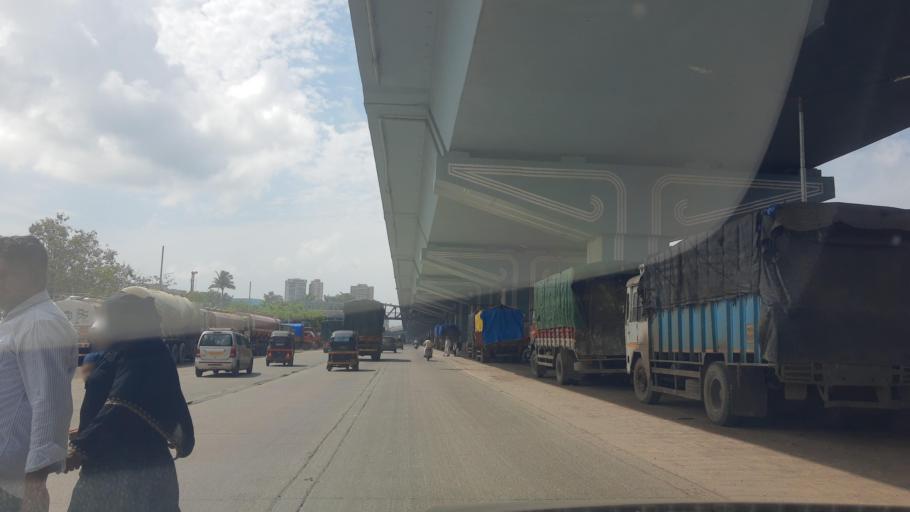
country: IN
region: Maharashtra
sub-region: Mumbai Suburban
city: Mumbai
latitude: 19.0574
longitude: 72.9266
